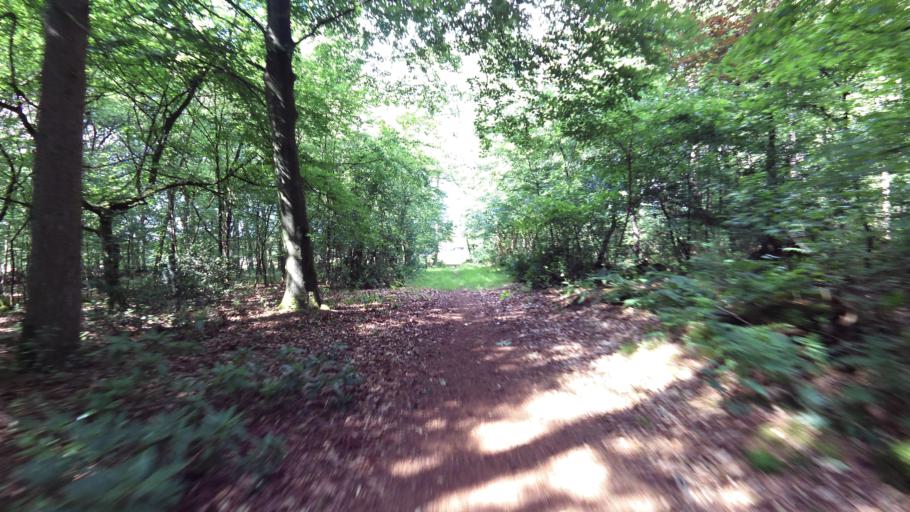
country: NL
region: Gelderland
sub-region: Gemeente Epe
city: Vaassen
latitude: 52.2722
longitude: 5.9284
